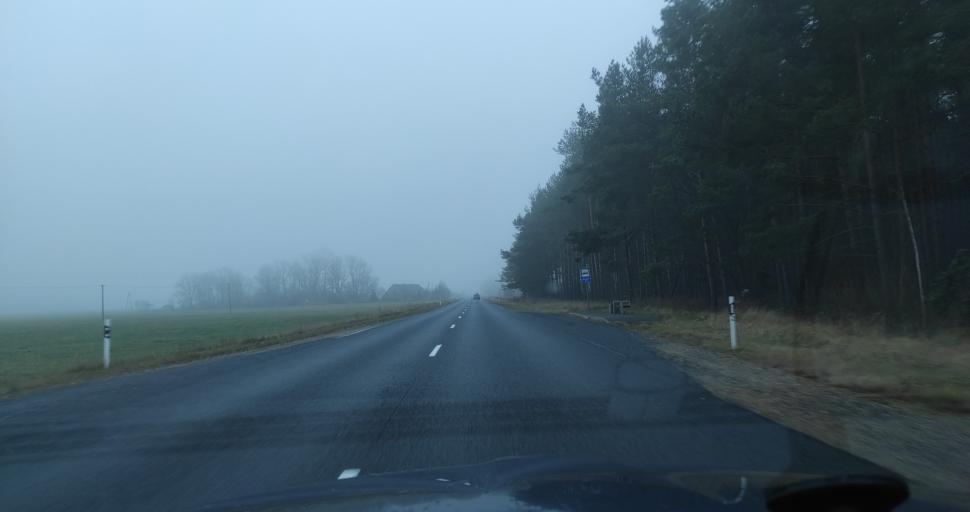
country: LV
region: Alsunga
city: Alsunga
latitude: 57.1044
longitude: 21.4228
